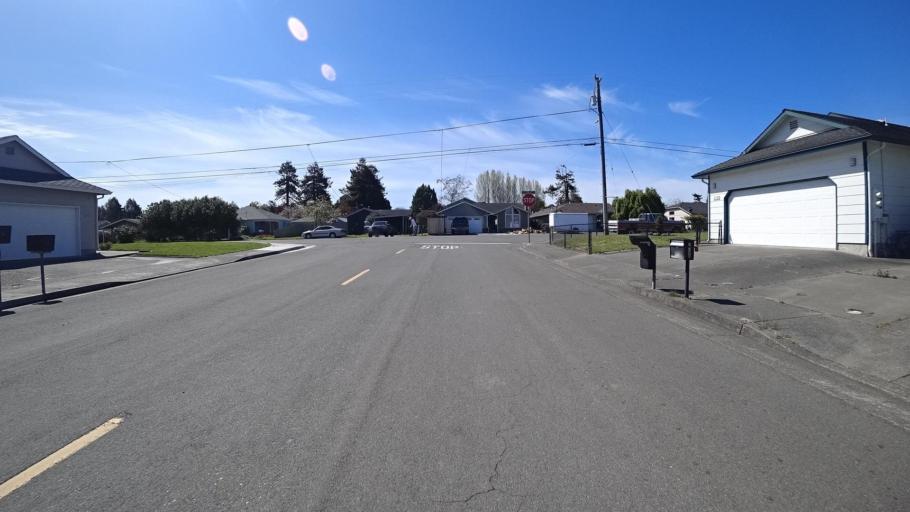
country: US
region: California
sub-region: Humboldt County
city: Myrtletown
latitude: 40.7868
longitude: -124.1263
